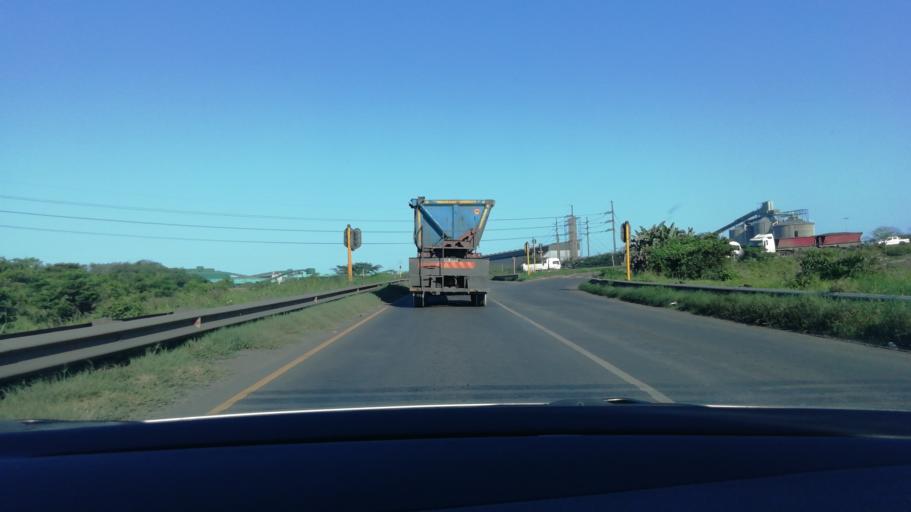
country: ZA
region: KwaZulu-Natal
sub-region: uThungulu District Municipality
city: Richards Bay
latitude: -28.7806
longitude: 32.0272
